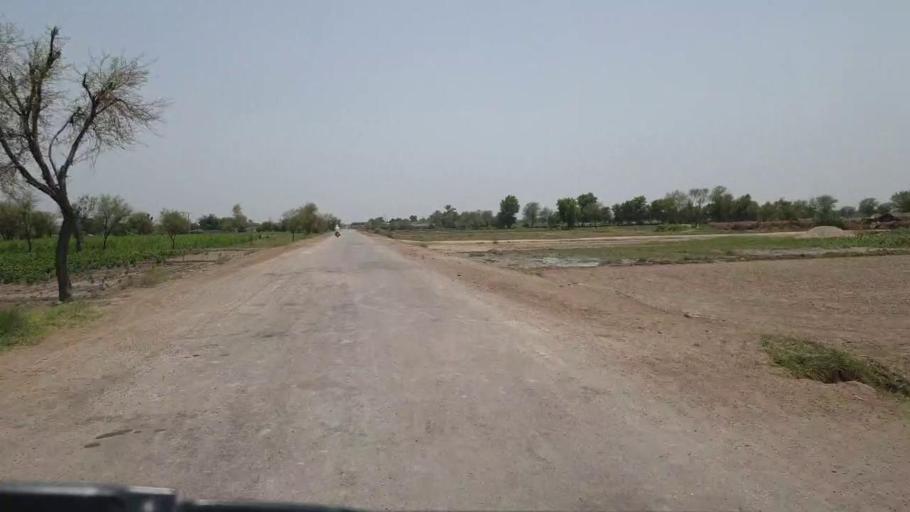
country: PK
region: Sindh
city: Daulatpur
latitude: 26.4475
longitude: 68.1165
